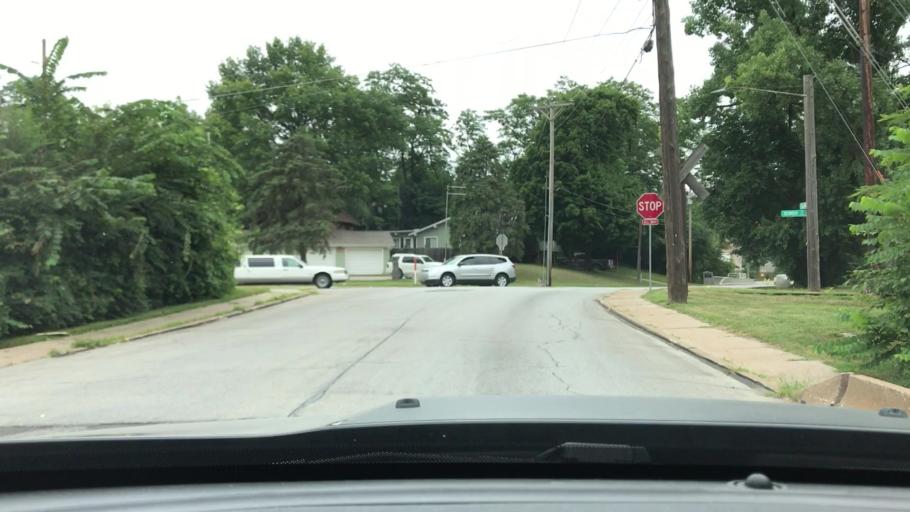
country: US
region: Illinois
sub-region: Rock Island County
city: Rock Island
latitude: 41.5169
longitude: -90.6221
